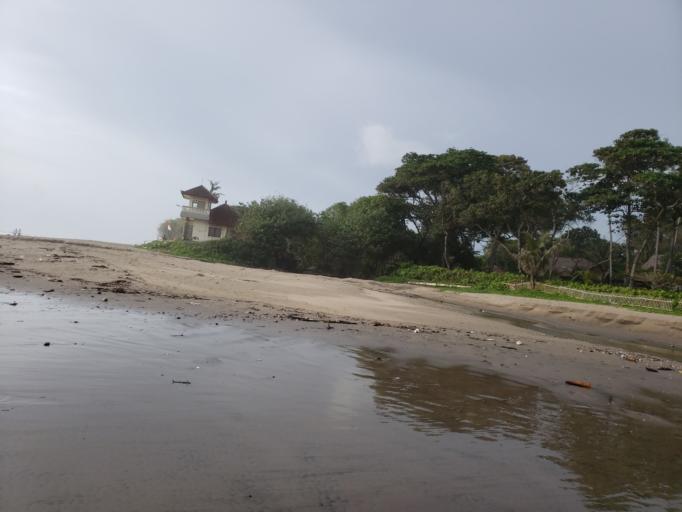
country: ID
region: Bali
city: Kuta
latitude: -8.6889
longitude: 115.1557
